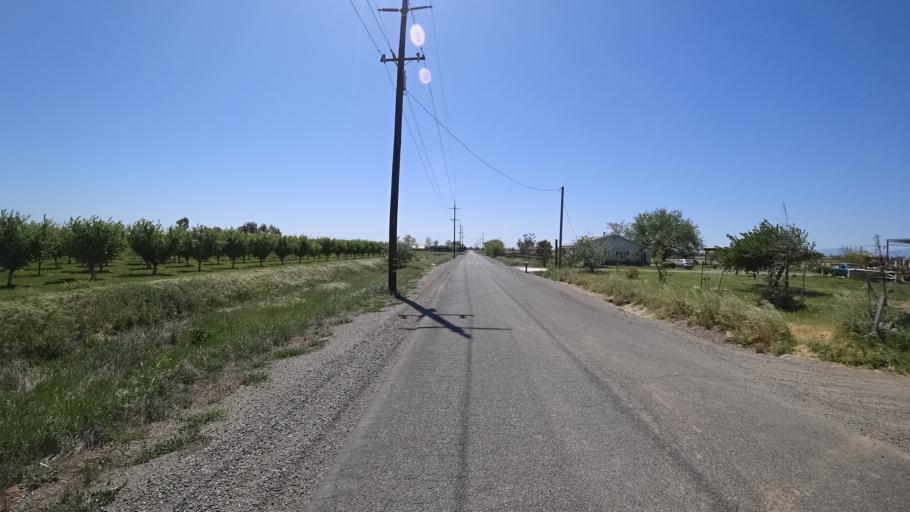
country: US
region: California
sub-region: Glenn County
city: Orland
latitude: 39.7748
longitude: -122.1409
